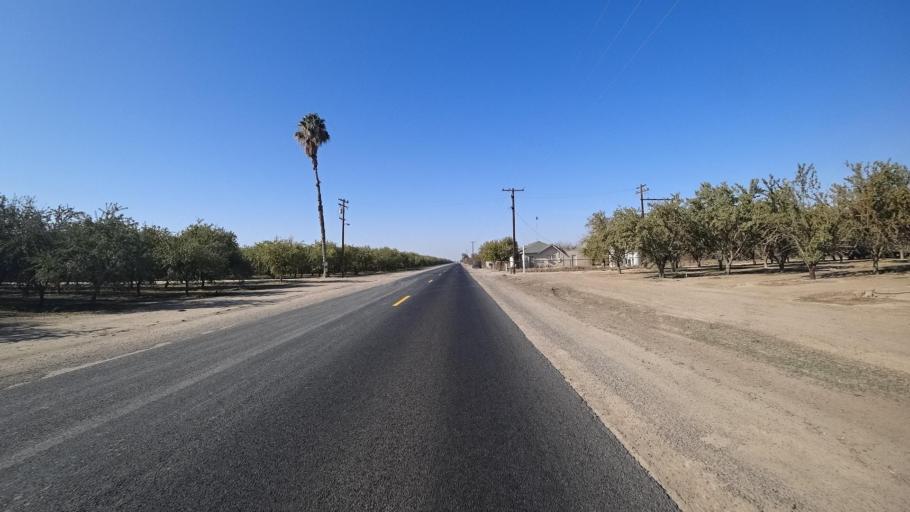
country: US
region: California
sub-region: Kern County
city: Wasco
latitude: 35.7177
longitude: -119.3743
